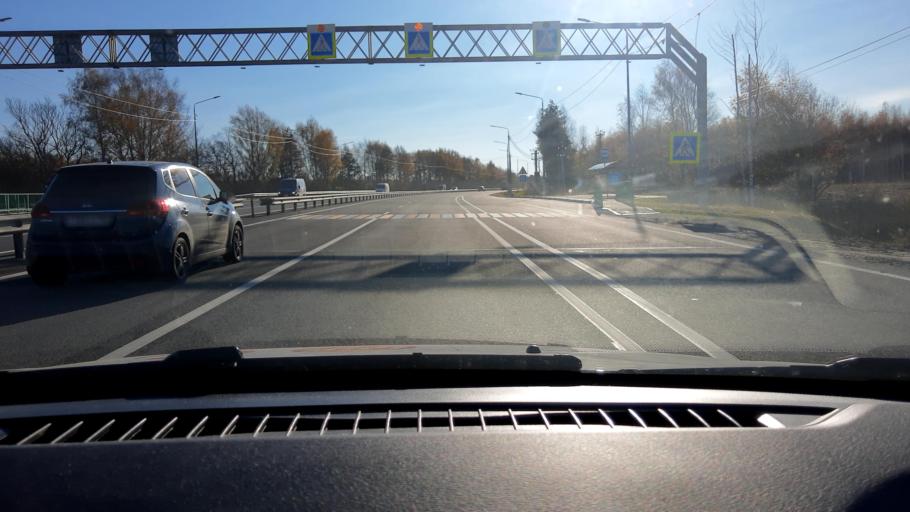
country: RU
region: Nizjnij Novgorod
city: Burevestnik
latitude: 56.0663
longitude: 43.9383
